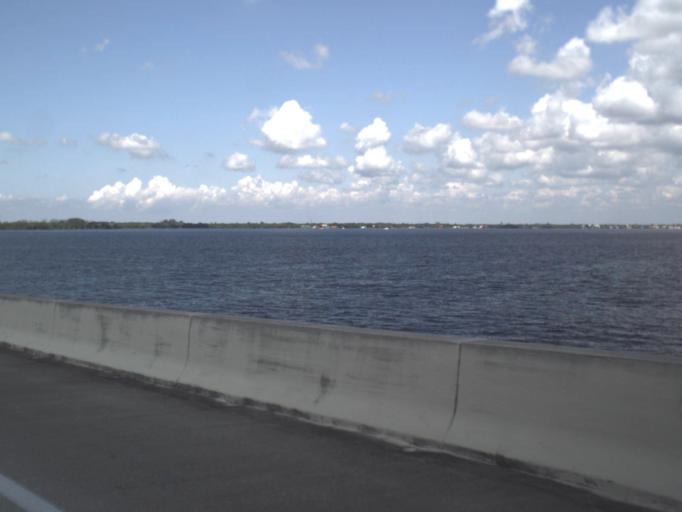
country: US
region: Florida
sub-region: Lee County
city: Whiskey Creek
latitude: 26.6034
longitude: -81.9042
